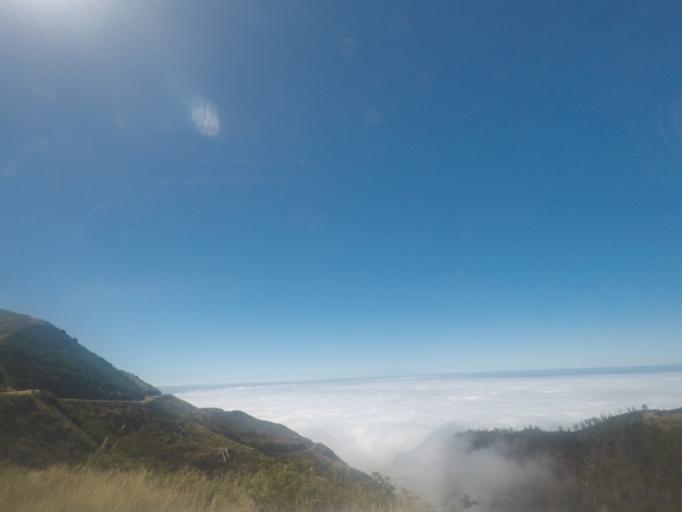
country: PT
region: Madeira
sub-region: Funchal
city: Nossa Senhora do Monte
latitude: 32.7071
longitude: -16.9175
